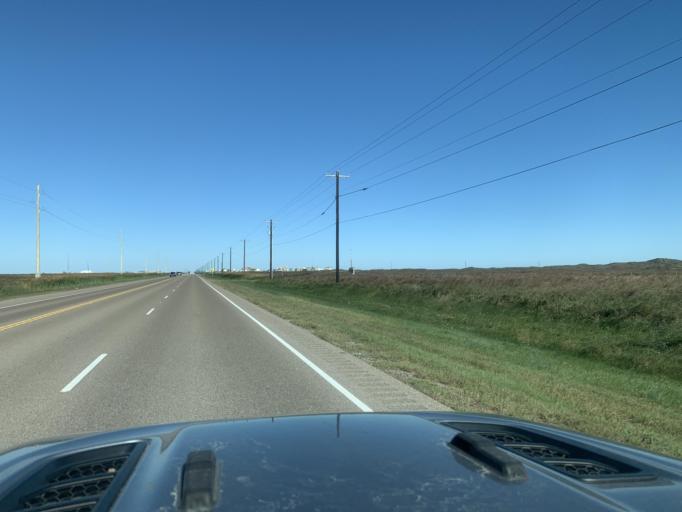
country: US
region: Texas
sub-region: Nueces County
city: Port Aransas
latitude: 27.7024
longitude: -97.1567
